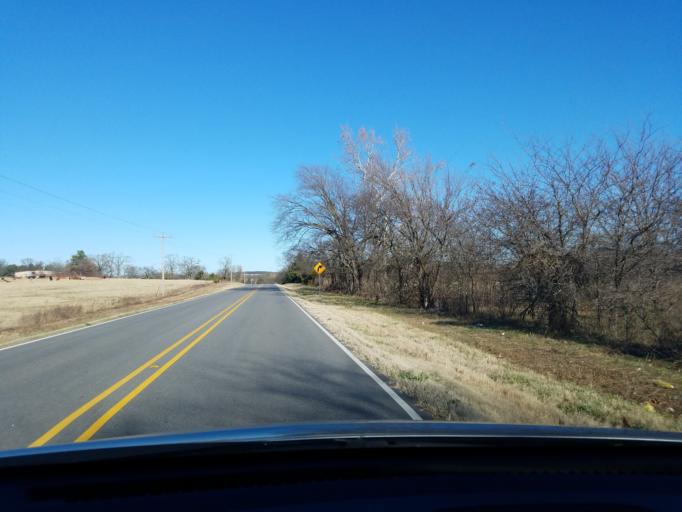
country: US
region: Arkansas
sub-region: Carroll County
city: Berryville
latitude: 36.3976
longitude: -93.5478
